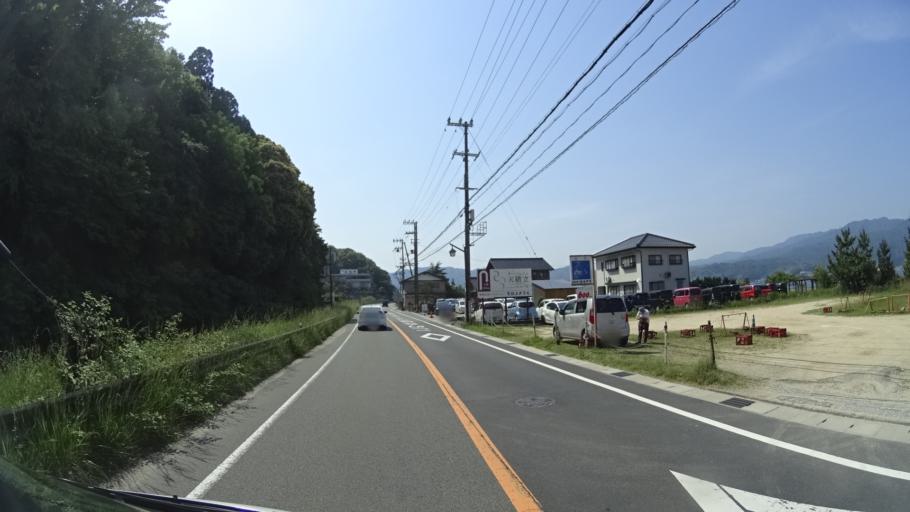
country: JP
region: Kyoto
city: Miyazu
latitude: 35.5590
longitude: 135.1804
